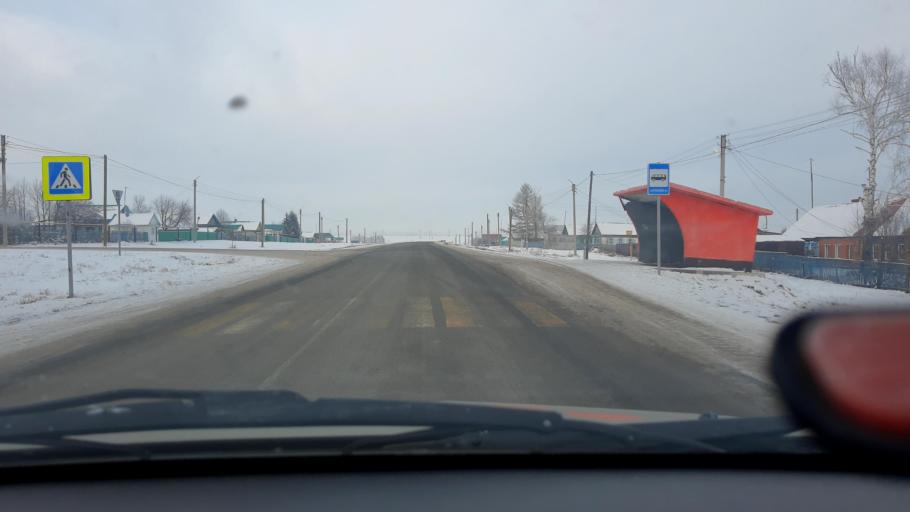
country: RU
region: Bashkortostan
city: Avdon
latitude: 54.3796
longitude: 55.8086
